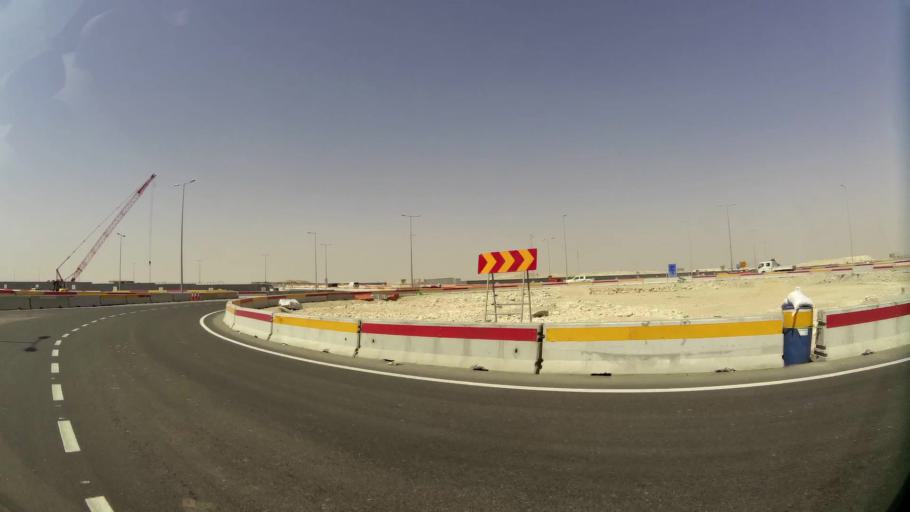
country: QA
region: Baladiyat Umm Salal
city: Umm Salal Muhammad
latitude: 25.3970
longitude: 51.4964
